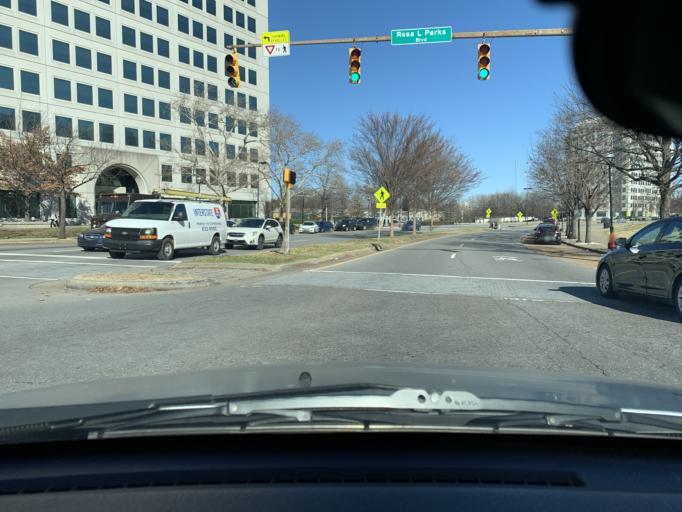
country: US
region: Tennessee
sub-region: Davidson County
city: Nashville
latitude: 36.1671
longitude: -86.7871
